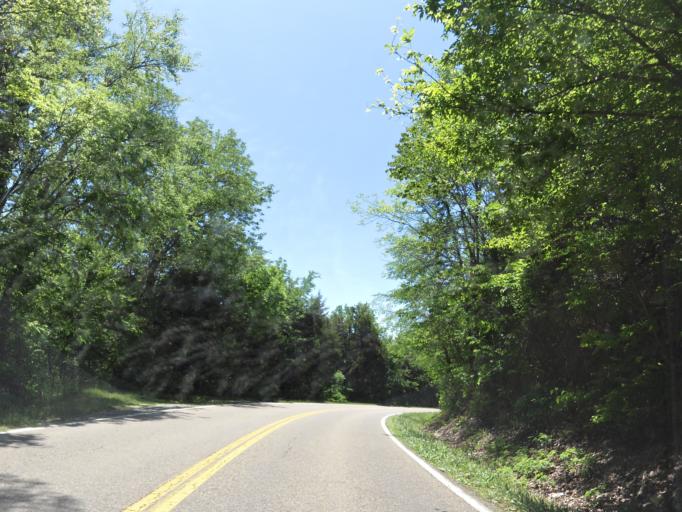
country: US
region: Tennessee
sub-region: Jefferson County
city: Dandridge
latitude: 35.9485
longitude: -83.3652
